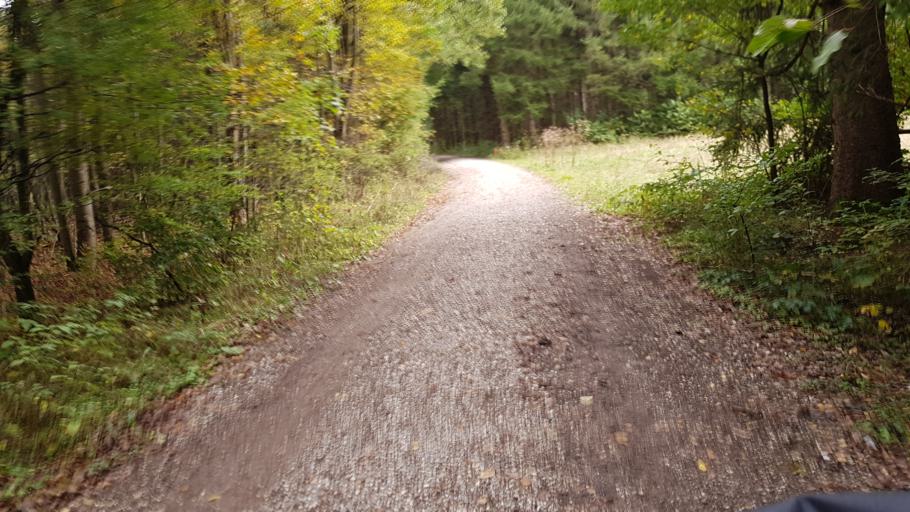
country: DE
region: Bavaria
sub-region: Upper Bavaria
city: Germering
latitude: 48.1063
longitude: 11.3465
